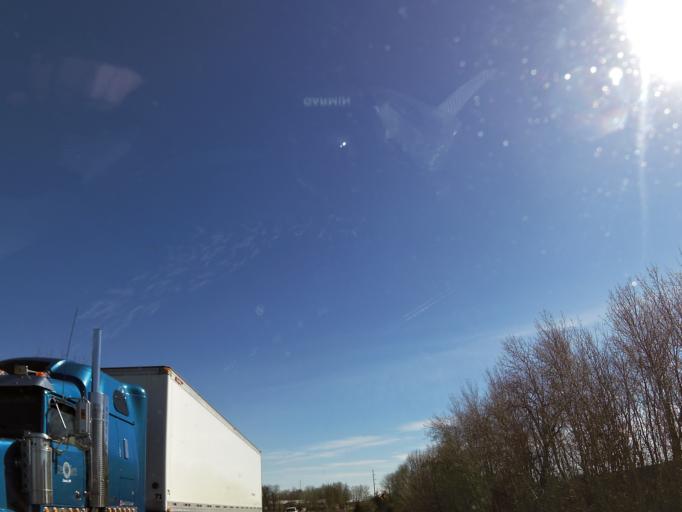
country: US
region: Minnesota
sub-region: Wright County
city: Delano
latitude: 45.1184
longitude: -93.8116
